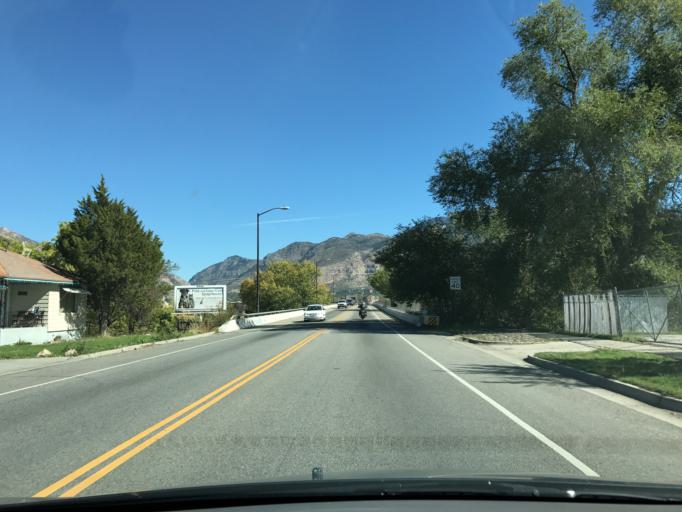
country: US
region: Utah
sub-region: Weber County
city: Ogden
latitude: 41.2229
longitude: -111.9893
